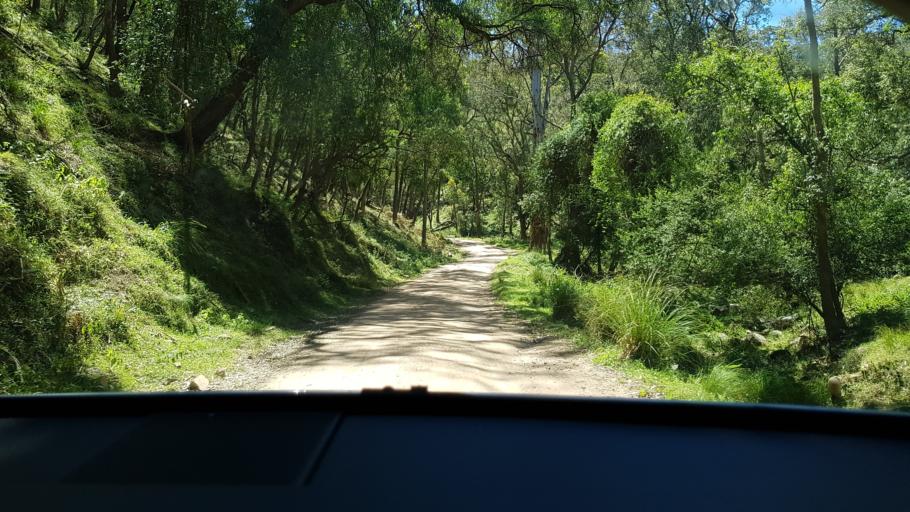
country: AU
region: New South Wales
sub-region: Blue Mountains Municipality
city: Katoomba
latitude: -33.7757
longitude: 150.2345
